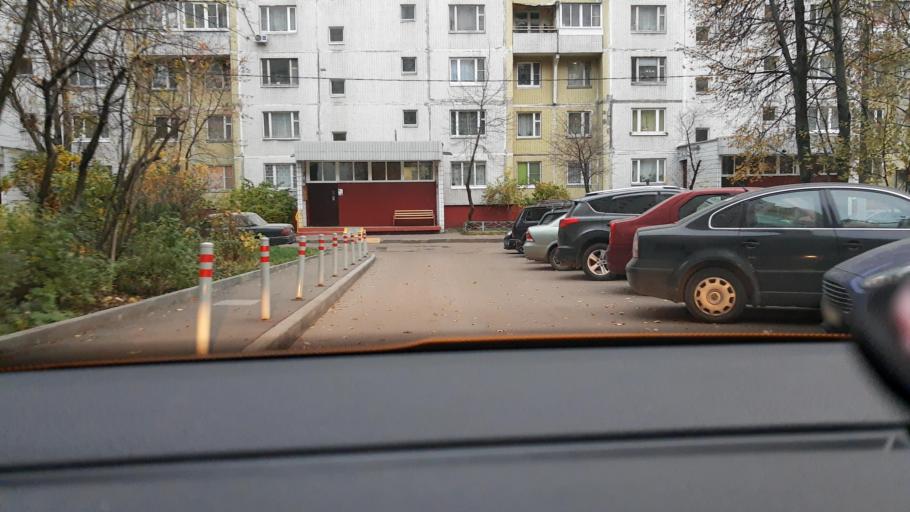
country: RU
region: Moscow
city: Biryulevo
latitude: 55.5818
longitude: 37.6870
